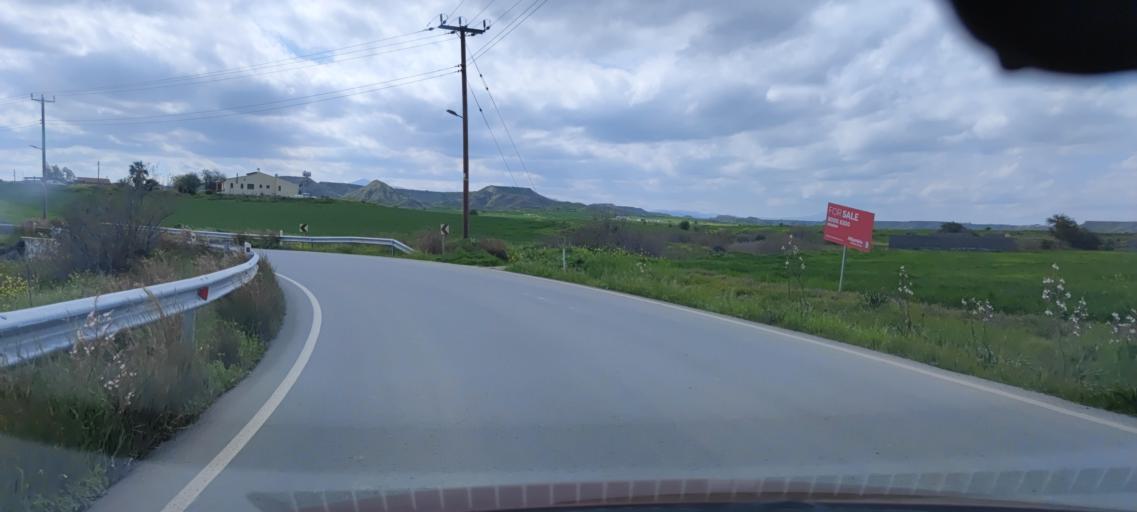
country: CY
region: Lefkosia
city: Tseri
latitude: 35.0476
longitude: 33.3185
